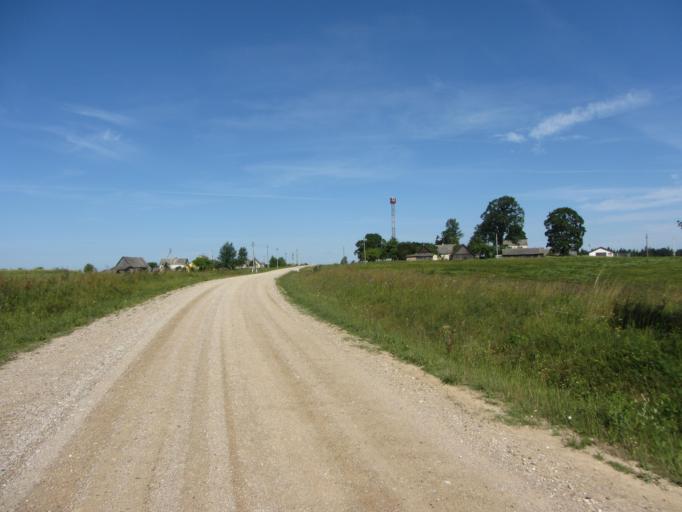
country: LT
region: Vilnius County
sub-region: Vilniaus Rajonas
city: Vievis
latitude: 54.8956
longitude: 24.7739
